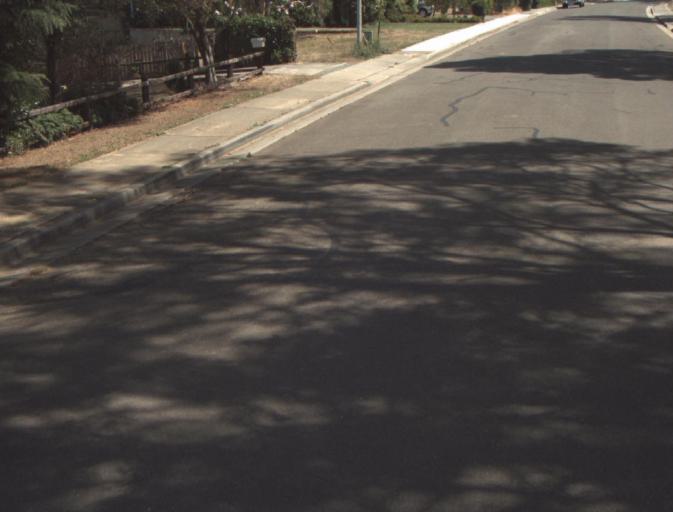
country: AU
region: Tasmania
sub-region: Launceston
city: Newstead
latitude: -41.4098
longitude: 147.1642
